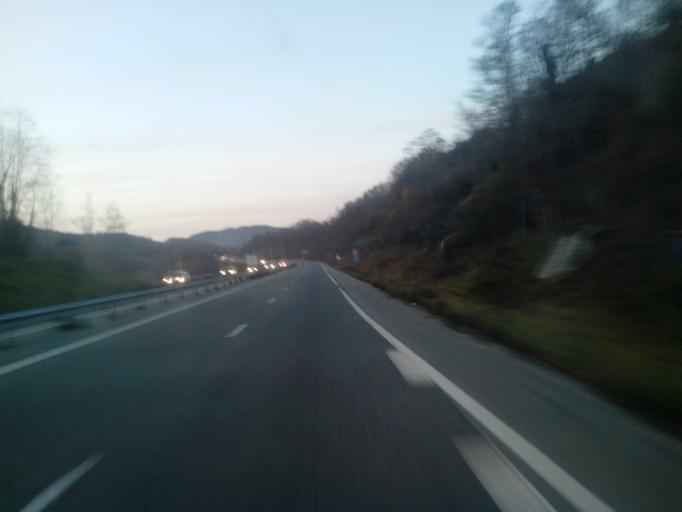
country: FR
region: Midi-Pyrenees
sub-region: Departement de l'Ariege
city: Montgaillard
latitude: 42.9259
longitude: 1.6339
